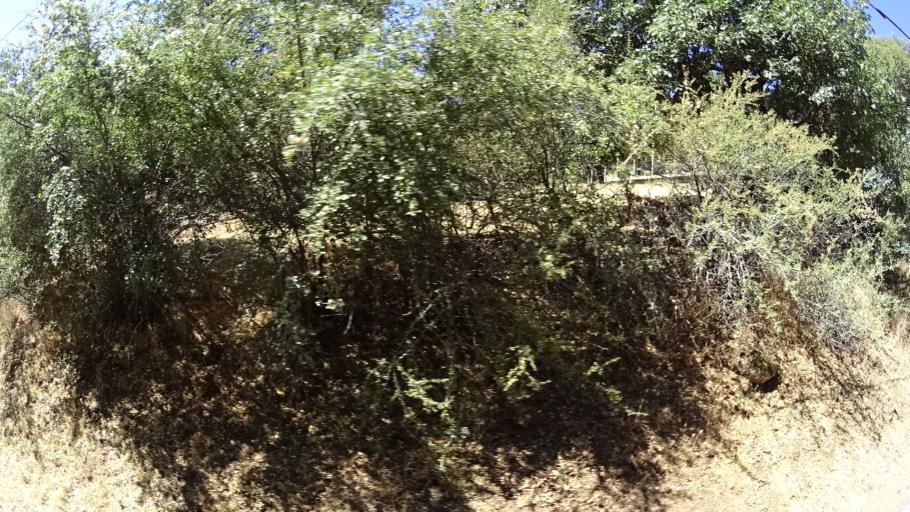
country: US
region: California
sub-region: Calaveras County
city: Forest Meadows
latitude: 38.1747
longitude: -120.3798
